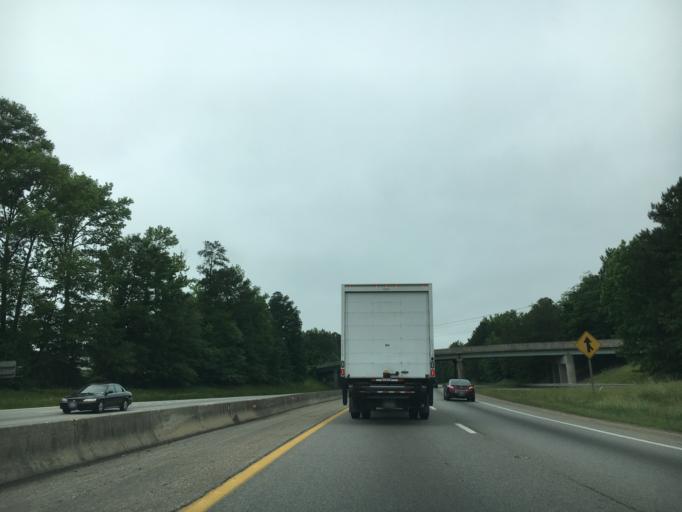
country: US
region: Virginia
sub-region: City of Petersburg
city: Petersburg
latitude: 37.1998
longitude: -77.4288
